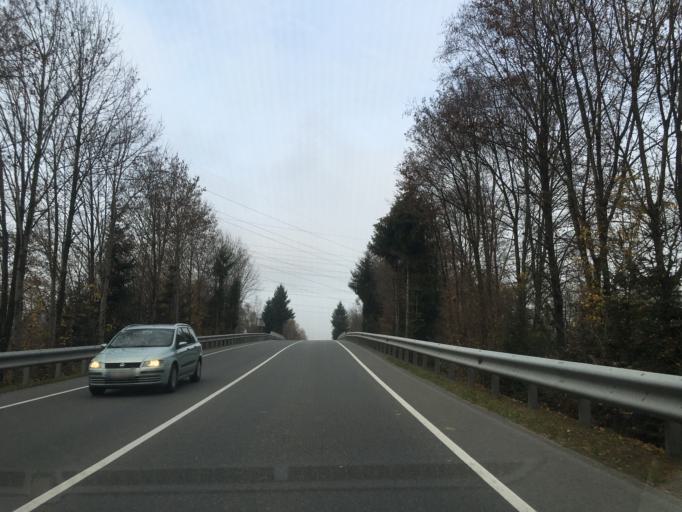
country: AT
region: Vorarlberg
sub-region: Politischer Bezirk Dornbirn
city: Hohenems
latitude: 47.3909
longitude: 9.6835
